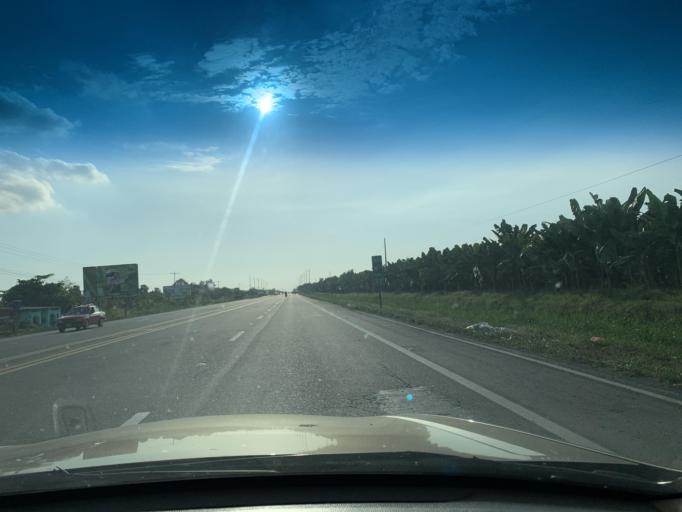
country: EC
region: Guayas
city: Naranjito
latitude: -2.2575
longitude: -79.5759
